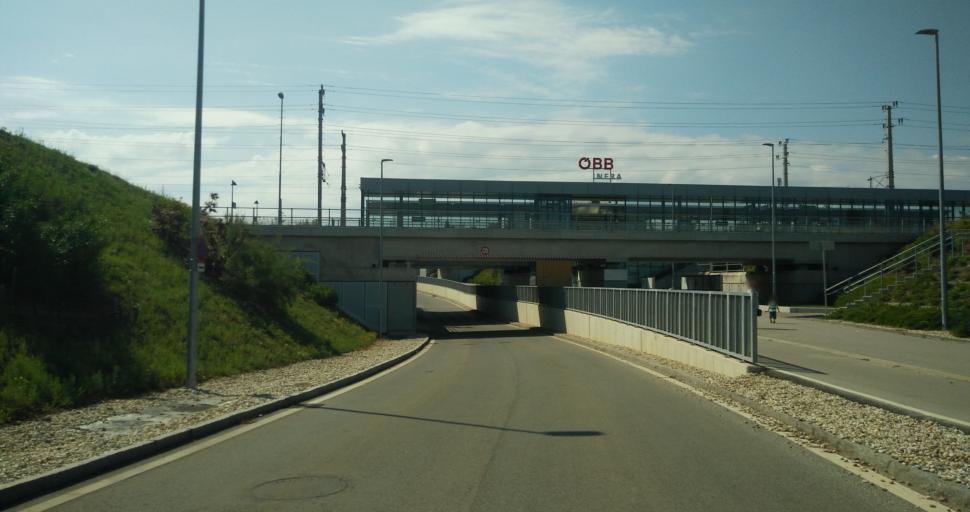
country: AT
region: Lower Austria
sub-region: Politischer Bezirk Ganserndorf
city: Strasshof an der Nordbahn
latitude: 48.3193
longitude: 16.6343
